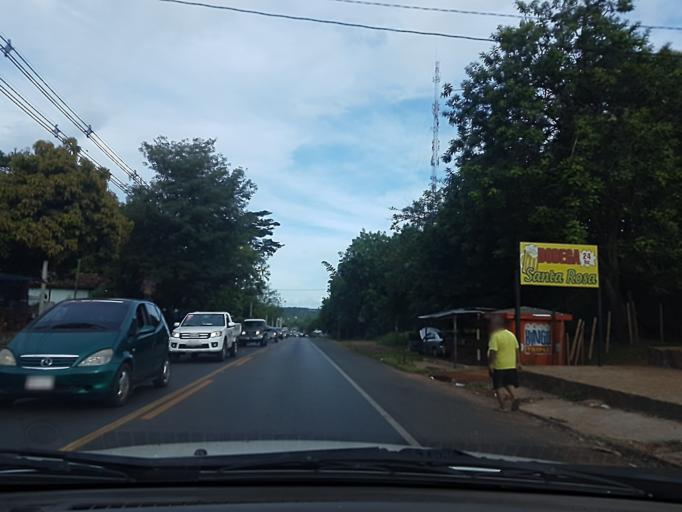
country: PY
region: Central
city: Capiata
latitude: -25.2892
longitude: -57.4562
